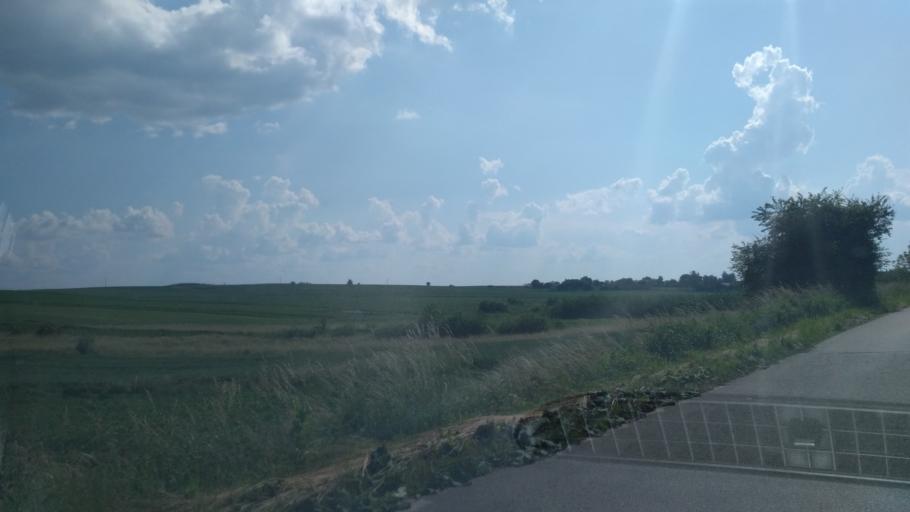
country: PL
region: Subcarpathian Voivodeship
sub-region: Powiat jaroslawski
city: Rokietnica
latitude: 49.9258
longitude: 22.7181
